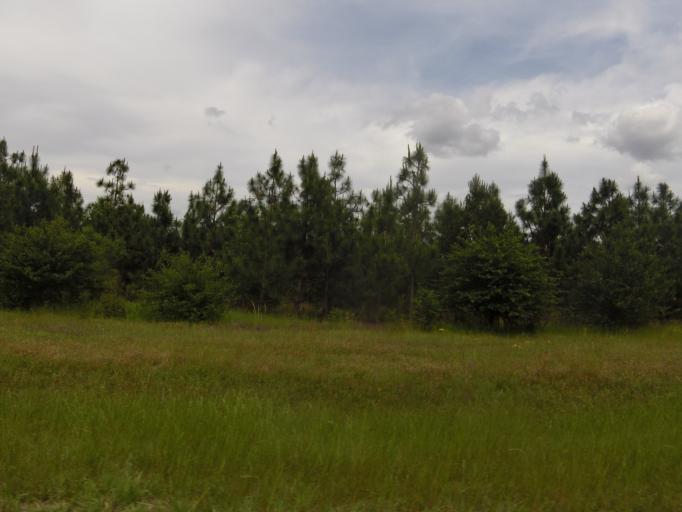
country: US
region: Georgia
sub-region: Jefferson County
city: Wrens
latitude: 33.2272
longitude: -82.4037
